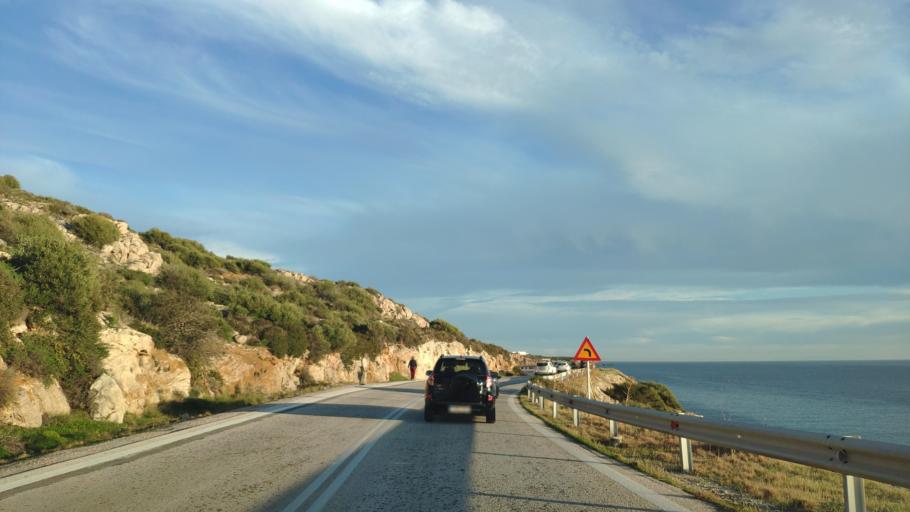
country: GR
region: Attica
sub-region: Nomarchia Anatolikis Attikis
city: Palaia Fokaia
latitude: 37.6664
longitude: 23.9623
